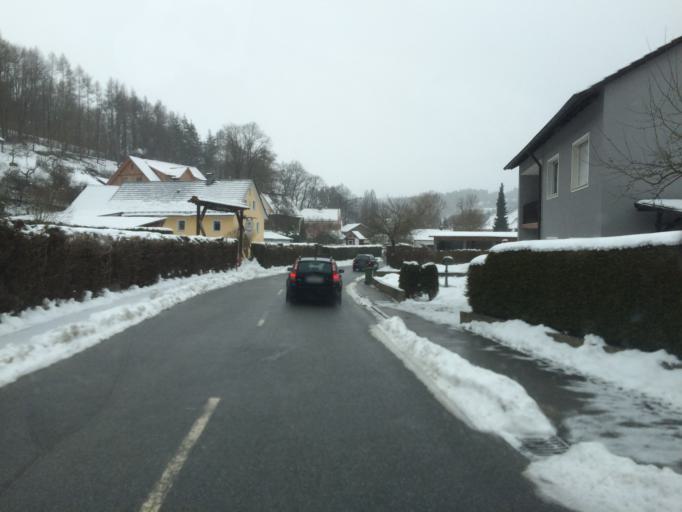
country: DE
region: Bavaria
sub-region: Upper Palatinate
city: Ensdorf
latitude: 49.3431
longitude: 11.9390
